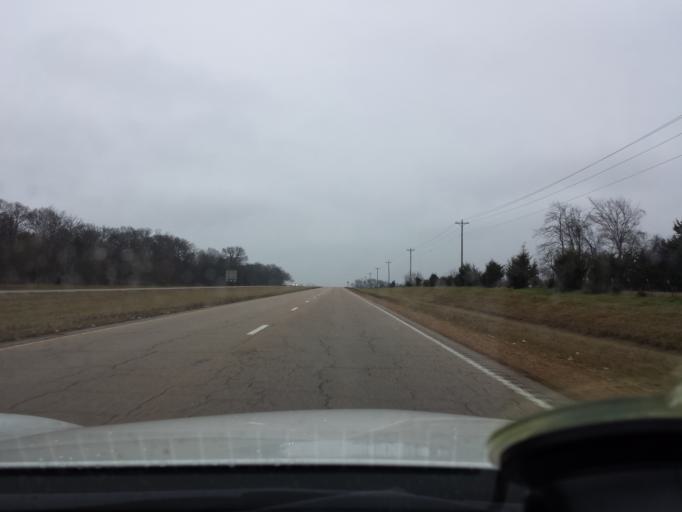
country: US
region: Mississippi
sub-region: Chickasaw County
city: Okolona
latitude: 34.0182
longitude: -88.7015
